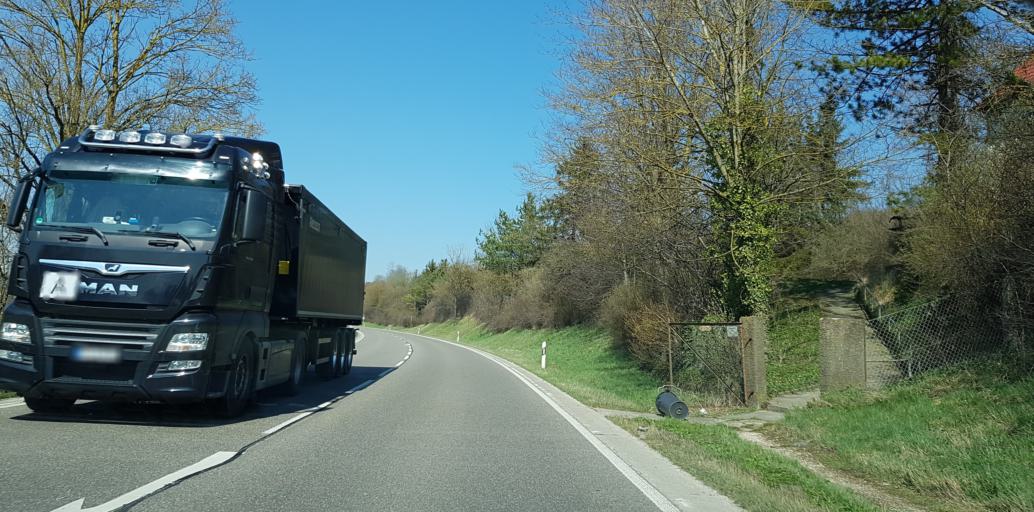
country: DE
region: Baden-Wuerttemberg
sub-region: Tuebingen Region
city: Ehingen
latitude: 48.2967
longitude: 9.7322
